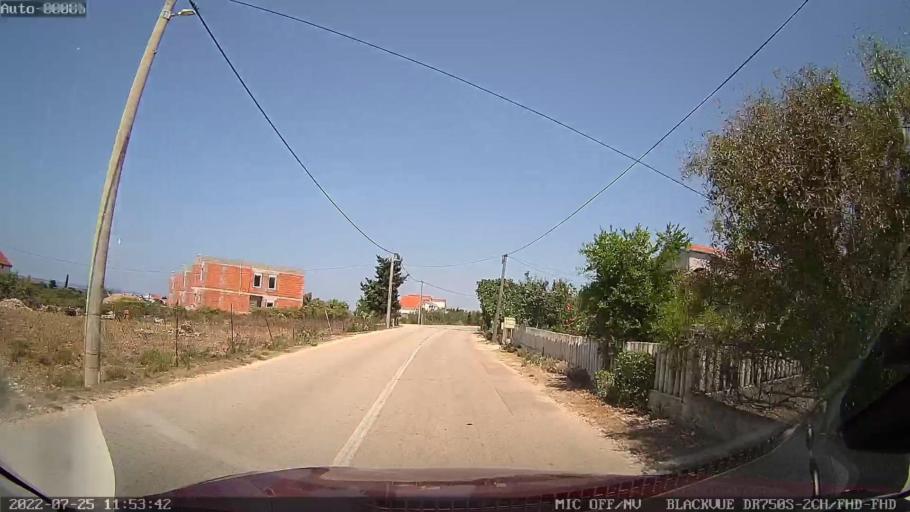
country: HR
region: Zadarska
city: Vrsi
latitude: 44.2576
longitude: 15.2338
